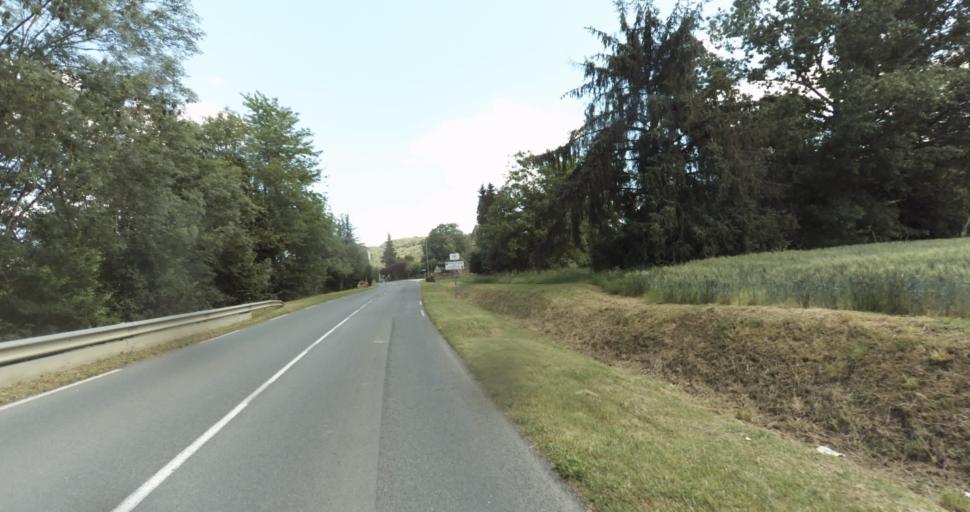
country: FR
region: Aquitaine
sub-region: Departement de la Dordogne
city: Lalinde
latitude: 44.8369
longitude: 0.7609
